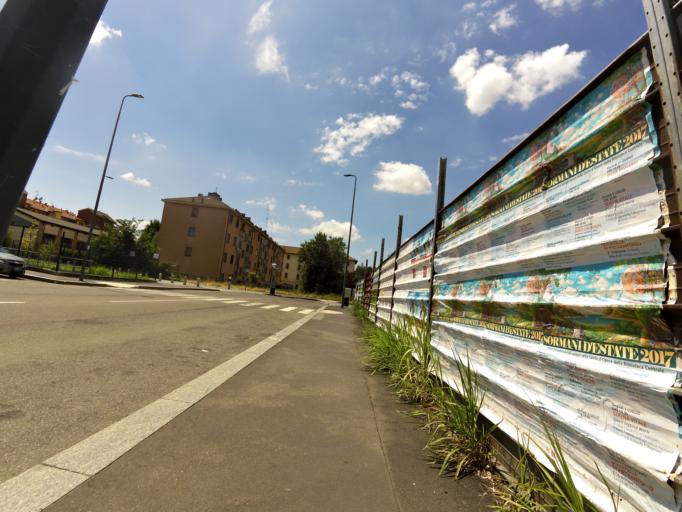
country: IT
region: Lombardy
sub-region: Citta metropolitana di Milano
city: Chiaravalle
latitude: 45.4338
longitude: 9.2443
